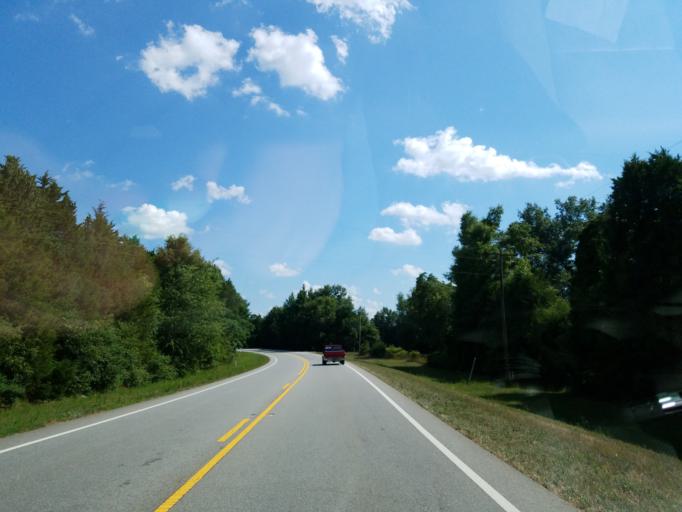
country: US
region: Georgia
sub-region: Lamar County
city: Barnesville
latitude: 32.9942
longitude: -84.1223
